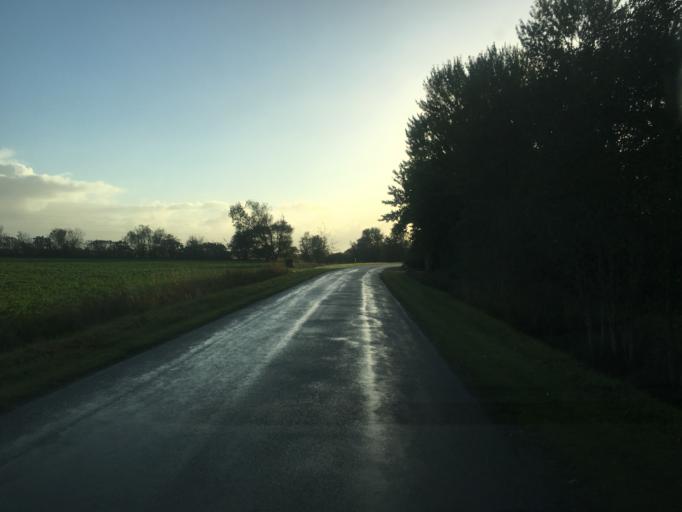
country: DE
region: Schleswig-Holstein
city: Aventoft
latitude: 54.9479
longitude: 8.7631
